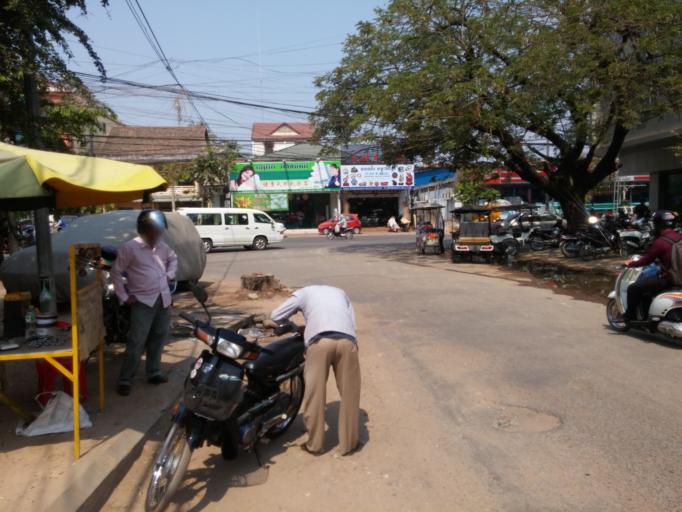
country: KH
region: Siem Reap
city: Siem Reap
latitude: 13.3573
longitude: 103.8544
